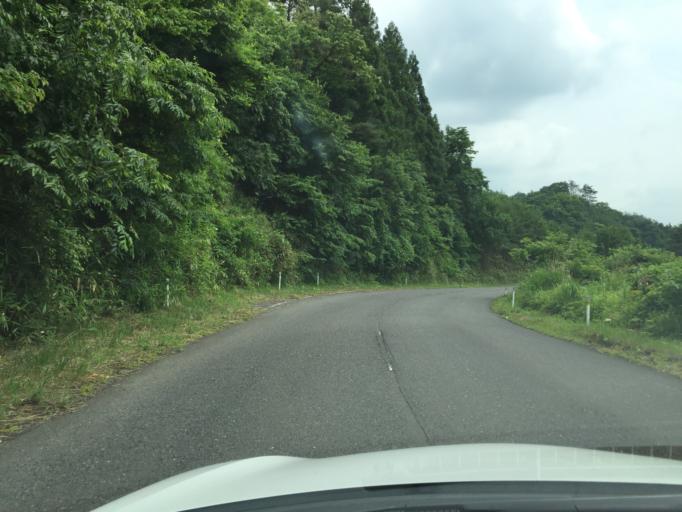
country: JP
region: Fukushima
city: Ishikawa
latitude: 37.2247
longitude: 140.4903
